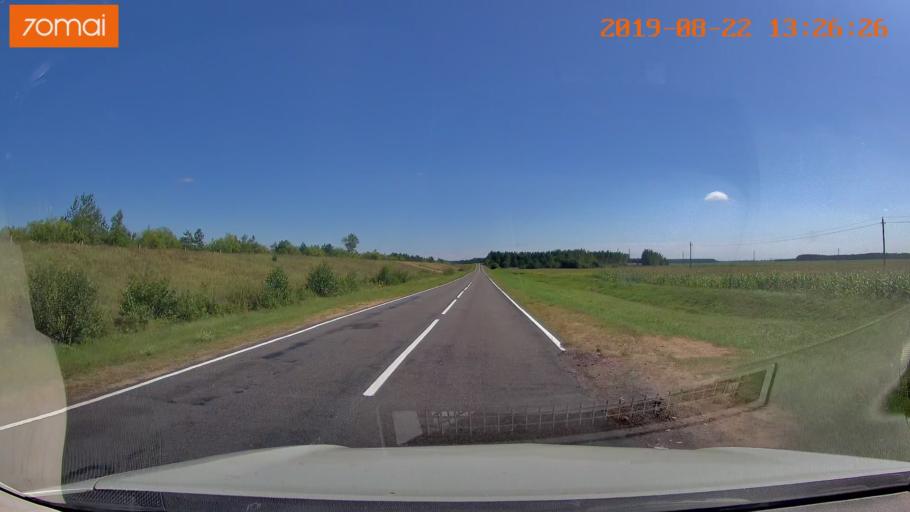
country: BY
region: Minsk
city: Staryya Darohi
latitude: 53.2096
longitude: 28.0619
